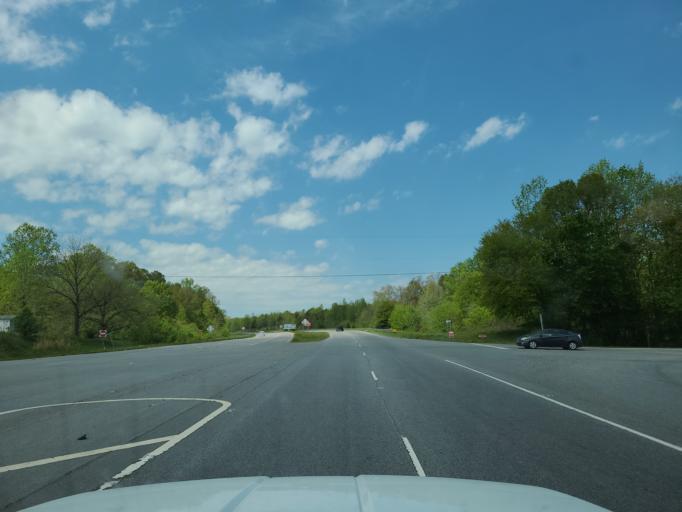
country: US
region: North Carolina
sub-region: Lincoln County
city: Lincolnton
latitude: 35.4265
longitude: -81.3036
